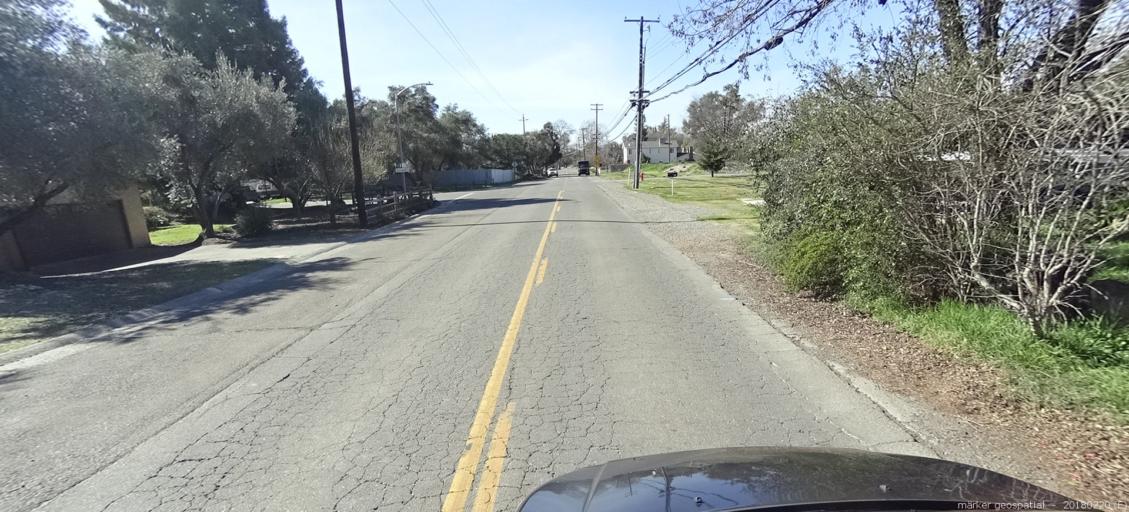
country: US
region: California
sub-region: Sacramento County
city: Orangevale
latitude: 38.6928
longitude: -121.2122
